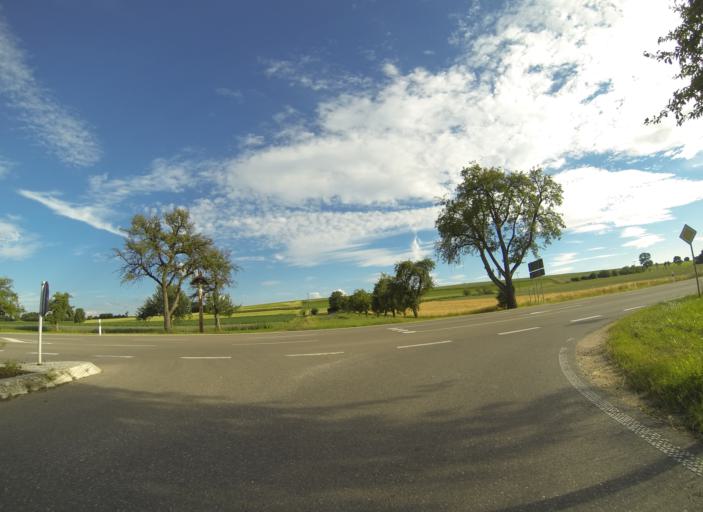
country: DE
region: Baden-Wuerttemberg
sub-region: Tuebingen Region
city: Altheim
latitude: 48.3237
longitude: 9.7685
